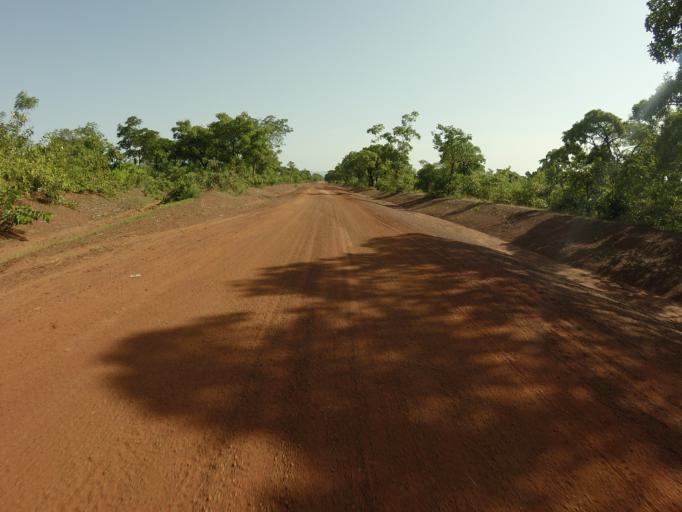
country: GH
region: Upper East
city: Bawku
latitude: 10.7348
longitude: -0.2032
